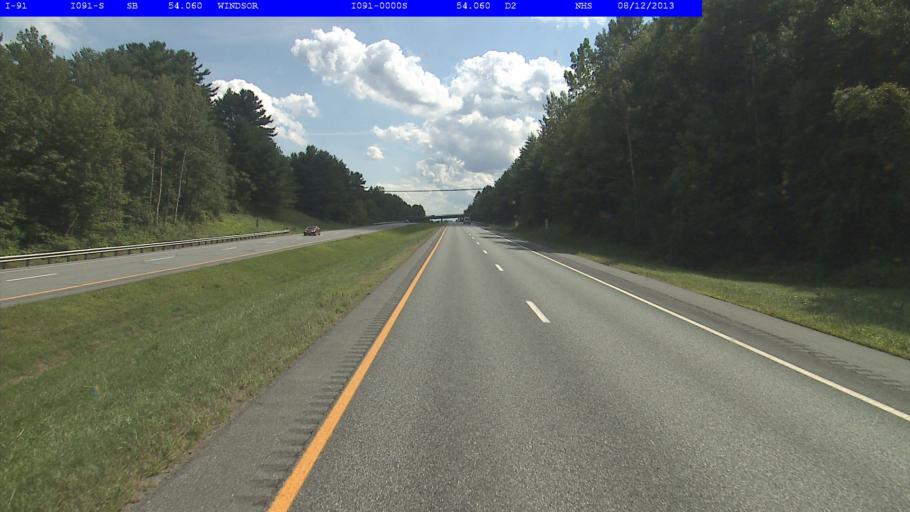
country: US
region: Vermont
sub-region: Windsor County
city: Windsor
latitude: 43.4388
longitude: -72.4029
